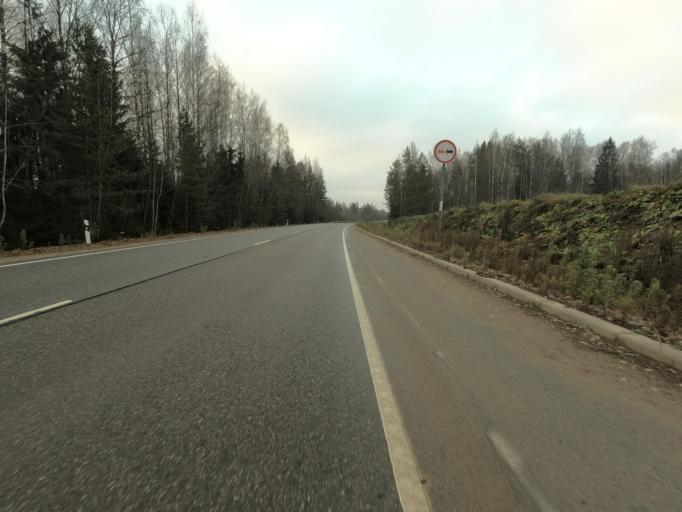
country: RU
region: Leningrad
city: Kirovsk
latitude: 59.8027
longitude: 30.9772
